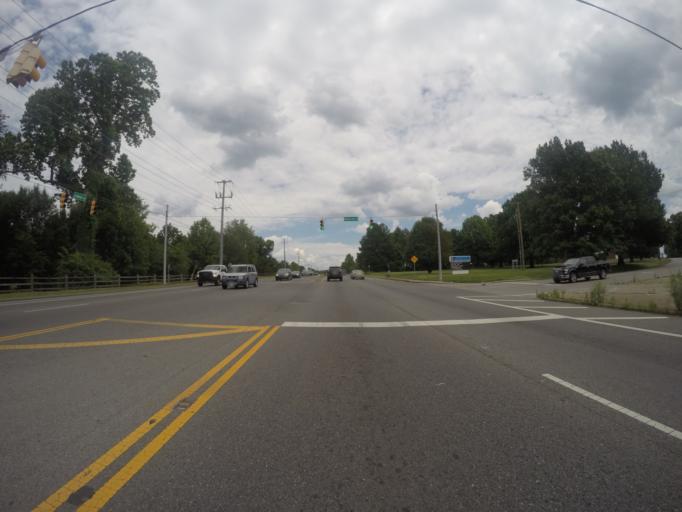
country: US
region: Tennessee
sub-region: Davidson County
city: Lakewood
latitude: 36.2075
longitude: -86.6118
